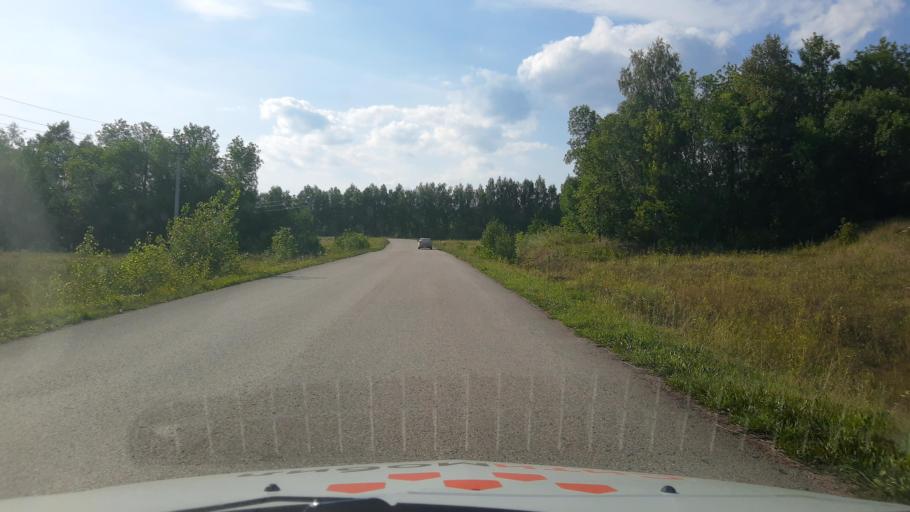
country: RU
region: Bashkortostan
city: Kabakovo
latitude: 54.6622
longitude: 56.1977
